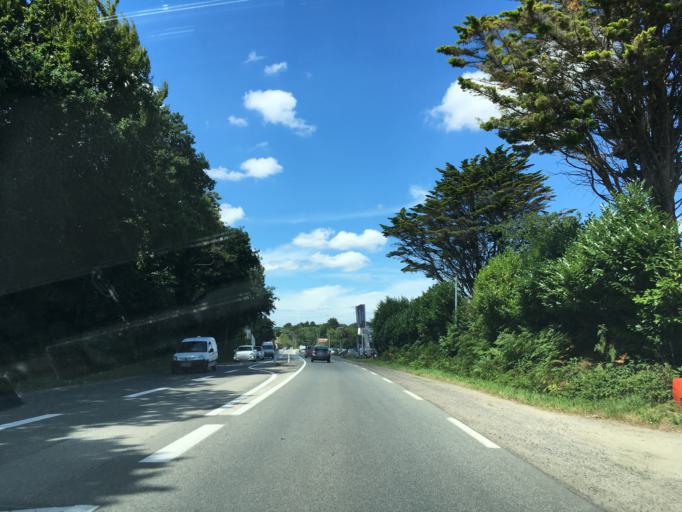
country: FR
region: Brittany
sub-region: Departement du Finistere
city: Quimper
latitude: 47.9680
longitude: -4.0846
